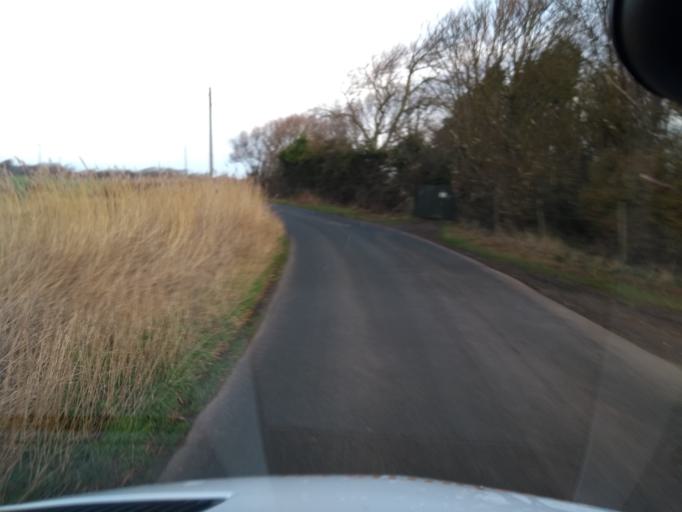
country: GB
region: England
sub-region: Somerset
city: Burnham-on-Sea
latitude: 51.2688
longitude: -3.0048
